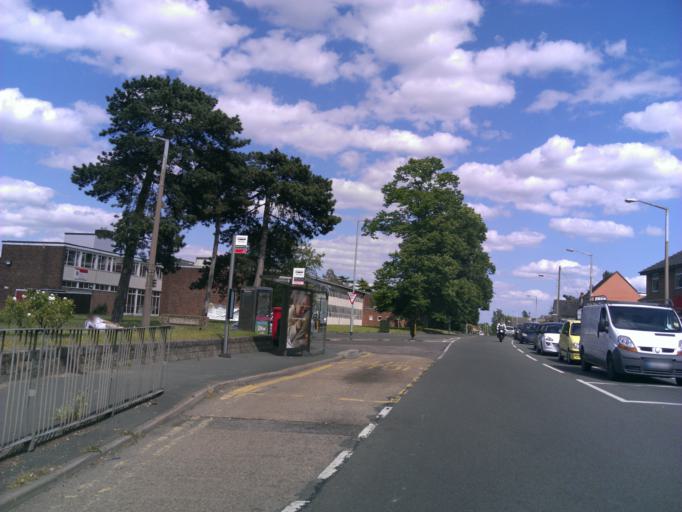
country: GB
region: England
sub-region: Essex
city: West Bergholt
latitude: 51.8898
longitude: 0.8524
